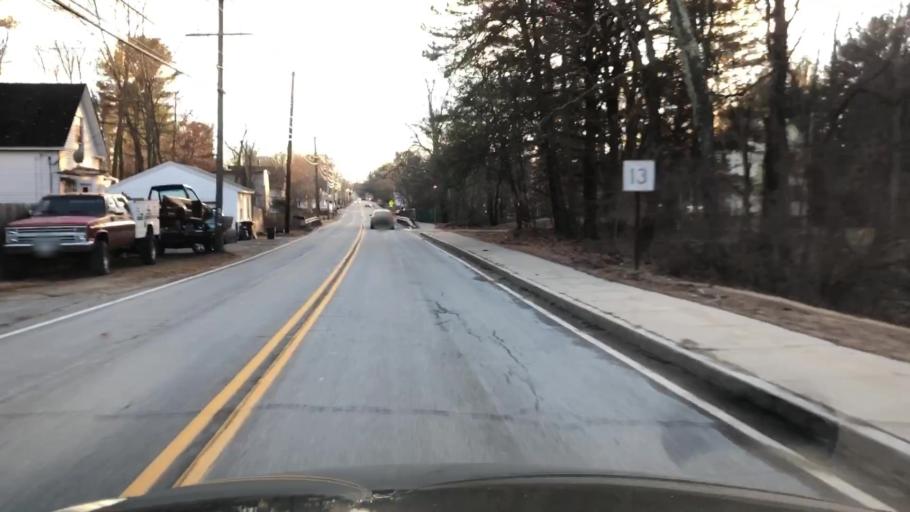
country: US
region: Massachusetts
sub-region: Middlesex County
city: Townsend
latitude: 42.6730
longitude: -71.6997
